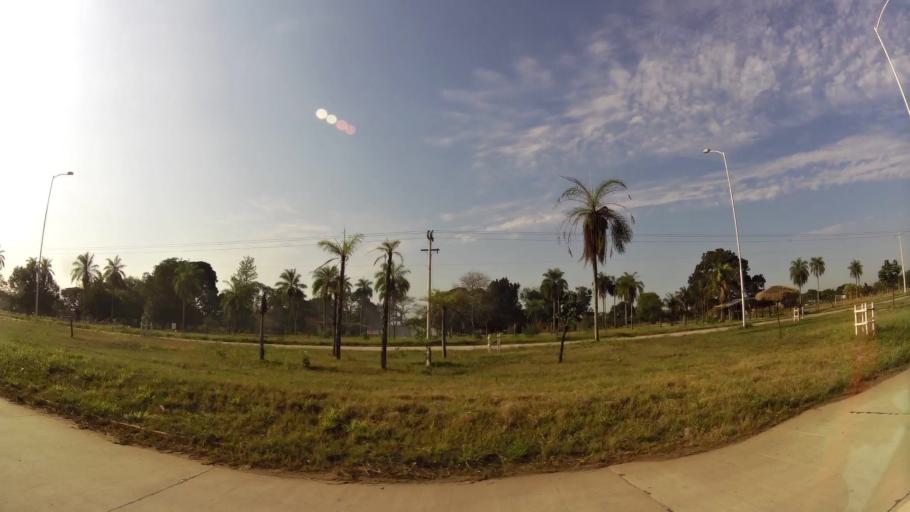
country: BO
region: Santa Cruz
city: Santa Cruz de la Sierra
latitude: -17.6984
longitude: -63.1251
